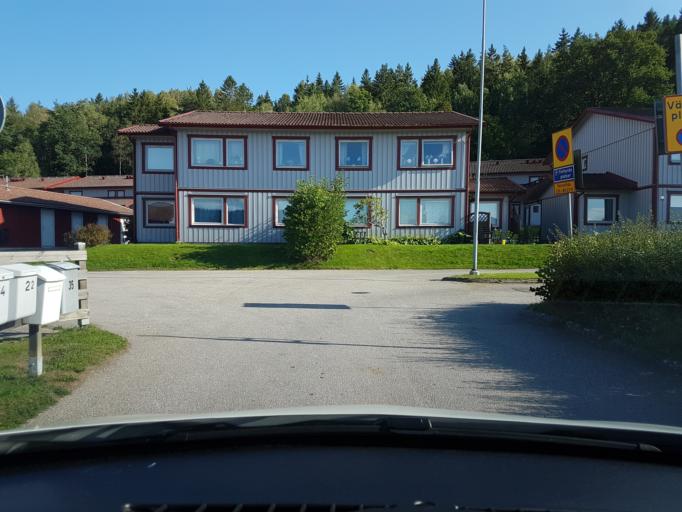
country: SE
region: Vaestra Goetaland
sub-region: Ale Kommun
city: Skepplanda
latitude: 57.9783
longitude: 12.1983
